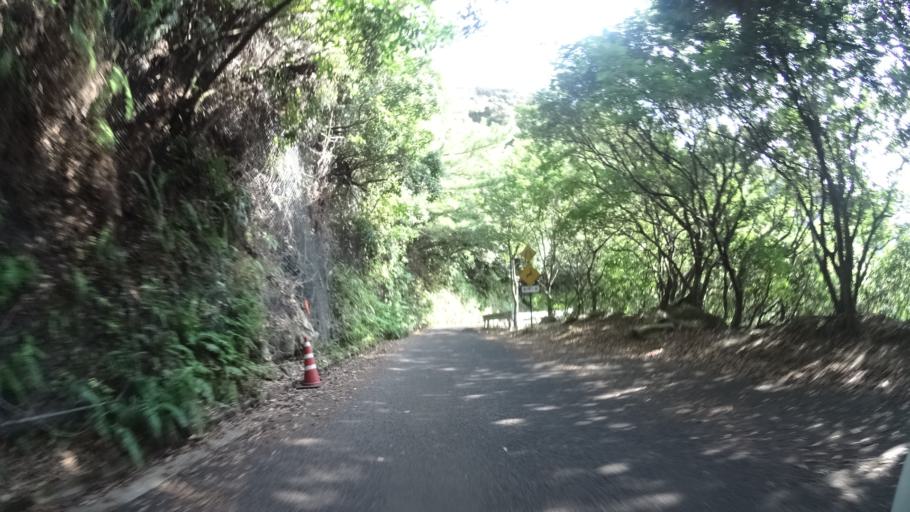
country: JP
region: Kagoshima
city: Nishinoomote
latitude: 30.3824
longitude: 130.3821
